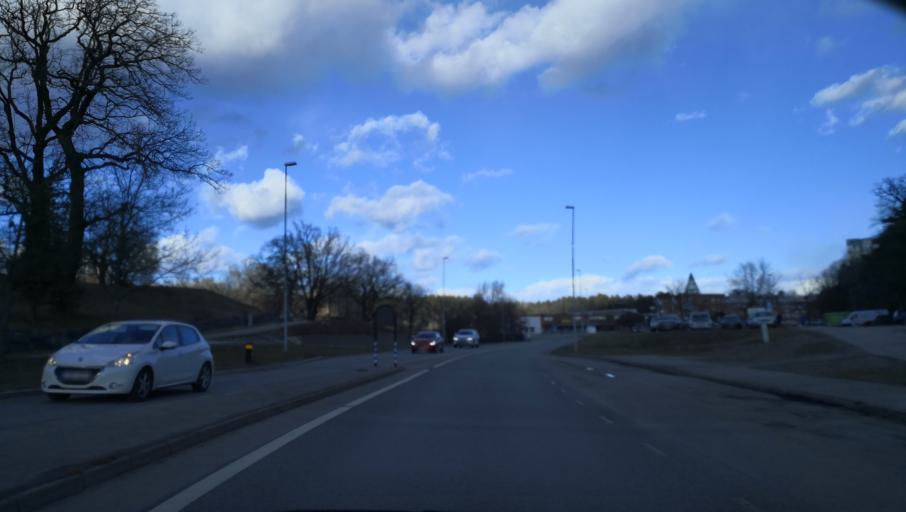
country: SE
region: Stockholm
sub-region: Varmdo Kommun
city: Gustavsberg
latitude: 59.3260
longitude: 18.3860
